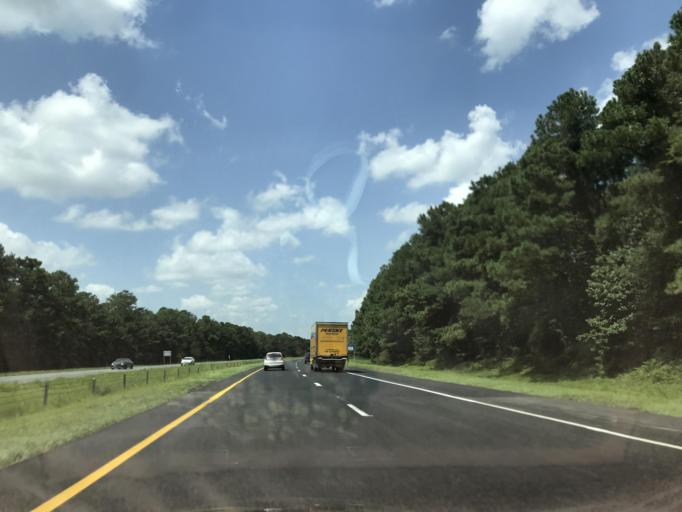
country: US
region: North Carolina
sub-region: Duplin County
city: Warsaw
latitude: 34.9721
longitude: -78.1207
